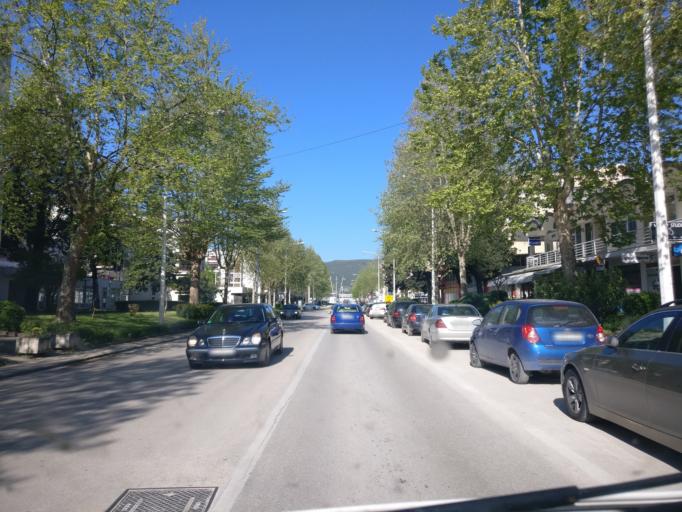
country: BA
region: Federation of Bosnia and Herzegovina
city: Tasovcici
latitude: 43.1095
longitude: 17.7030
